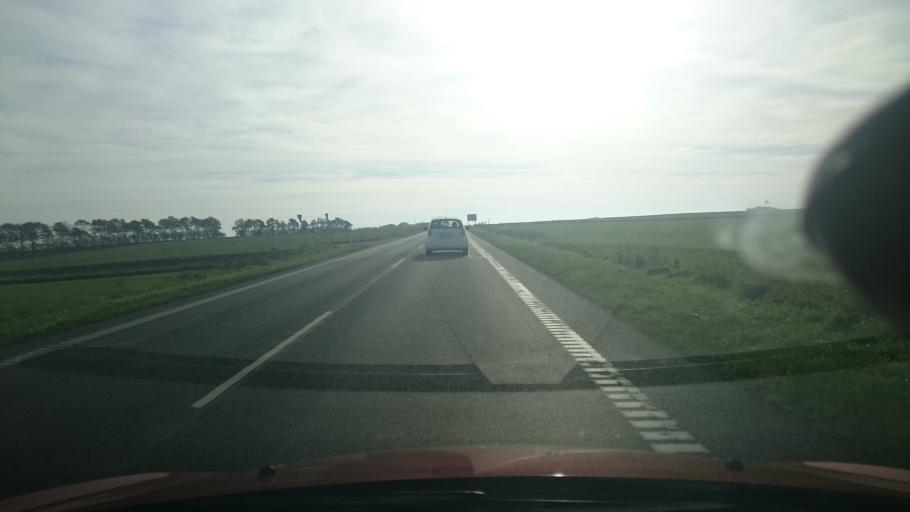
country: DK
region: Central Jutland
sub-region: Randers Kommune
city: Assentoft
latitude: 56.4179
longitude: 10.2145
